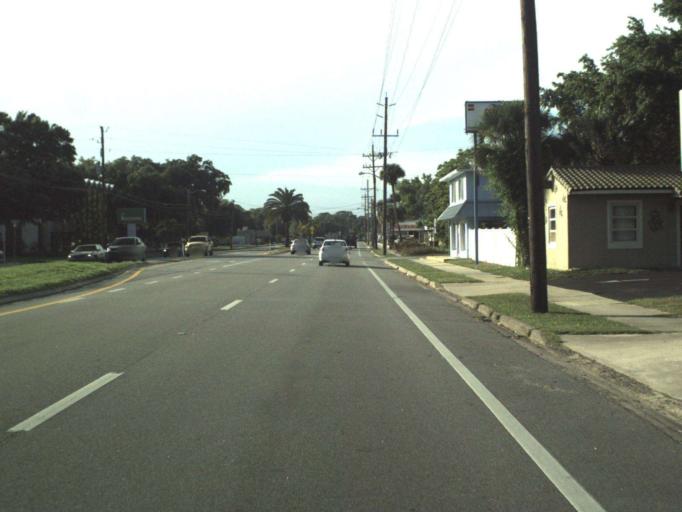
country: US
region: Florida
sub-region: Volusia County
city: New Smyrna Beach
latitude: 29.0376
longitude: -80.9323
